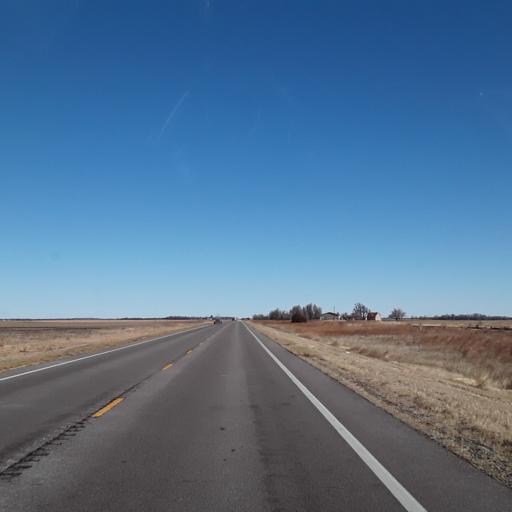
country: US
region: Kansas
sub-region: Pawnee County
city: Larned
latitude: 38.0927
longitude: -99.2185
